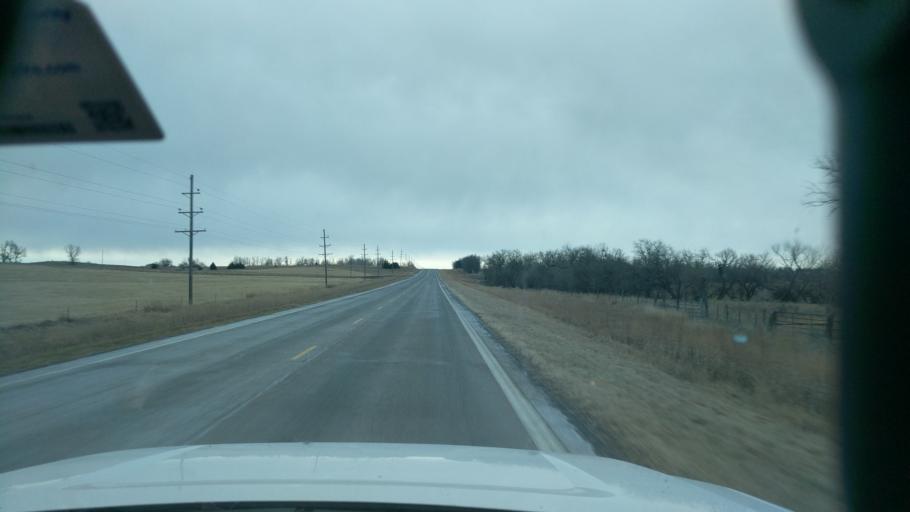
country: US
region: Kansas
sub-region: Marion County
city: Hillsboro
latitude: 38.3265
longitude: -97.3347
